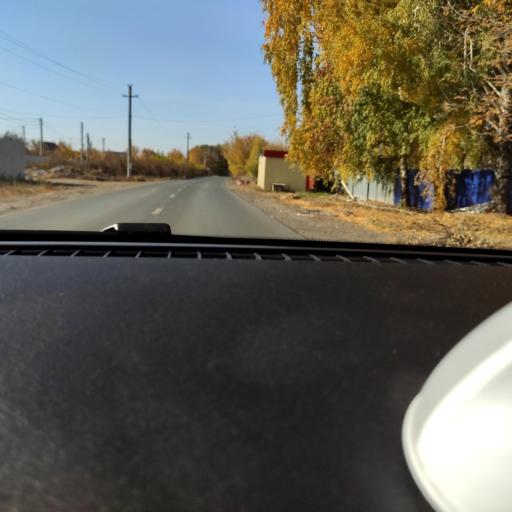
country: RU
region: Samara
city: Smyshlyayevka
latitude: 53.2429
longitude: 50.3564
